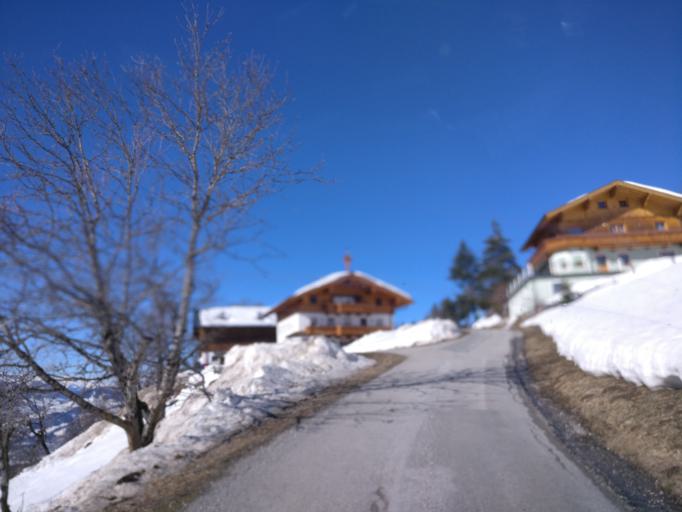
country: AT
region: Salzburg
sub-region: Politischer Bezirk Sankt Johann im Pongau
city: Sankt Johann im Pongau
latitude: 47.3369
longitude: 13.2285
